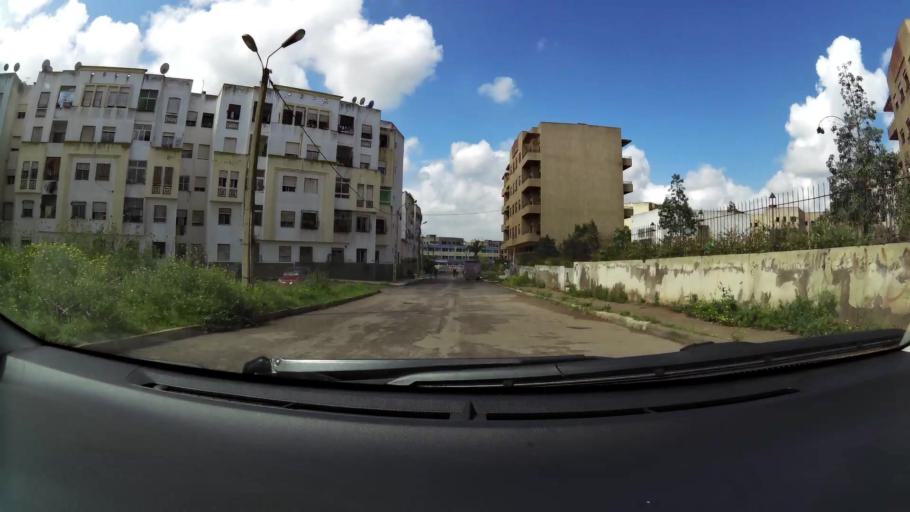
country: MA
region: Grand Casablanca
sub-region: Mediouna
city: Tit Mellil
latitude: 33.5539
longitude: -7.4797
